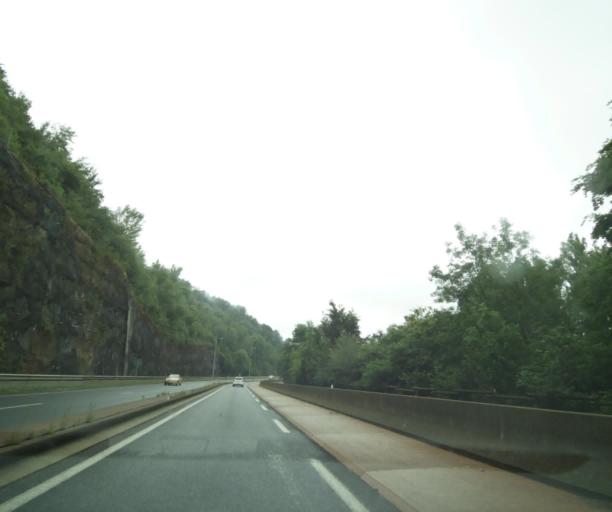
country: FR
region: Midi-Pyrenees
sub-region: Departement de l'Aveyron
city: Olemps
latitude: 44.3493
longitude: 2.5551
